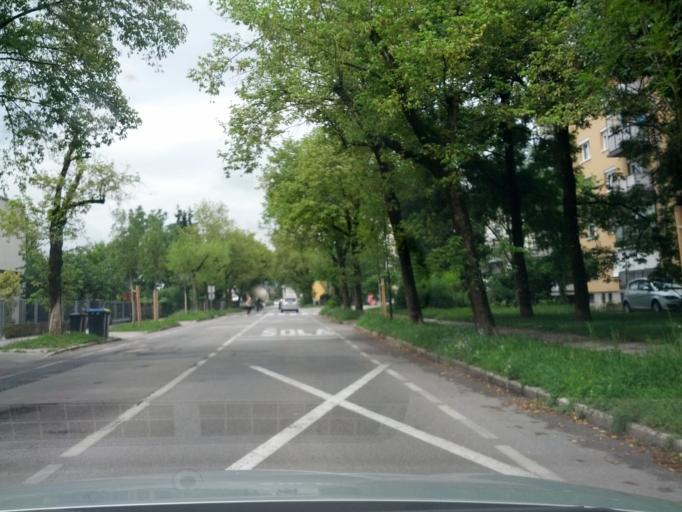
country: SI
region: Ljubljana
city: Ljubljana
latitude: 46.0719
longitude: 14.5076
